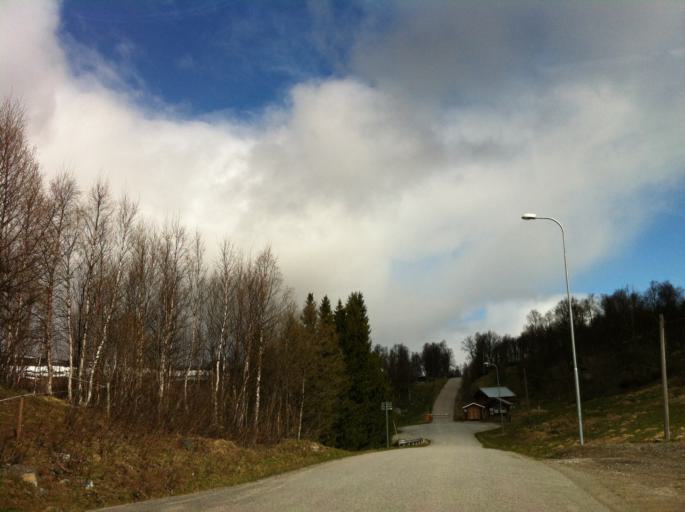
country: NO
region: Sor-Trondelag
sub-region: Tydal
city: Aas
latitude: 62.6394
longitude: 12.4443
